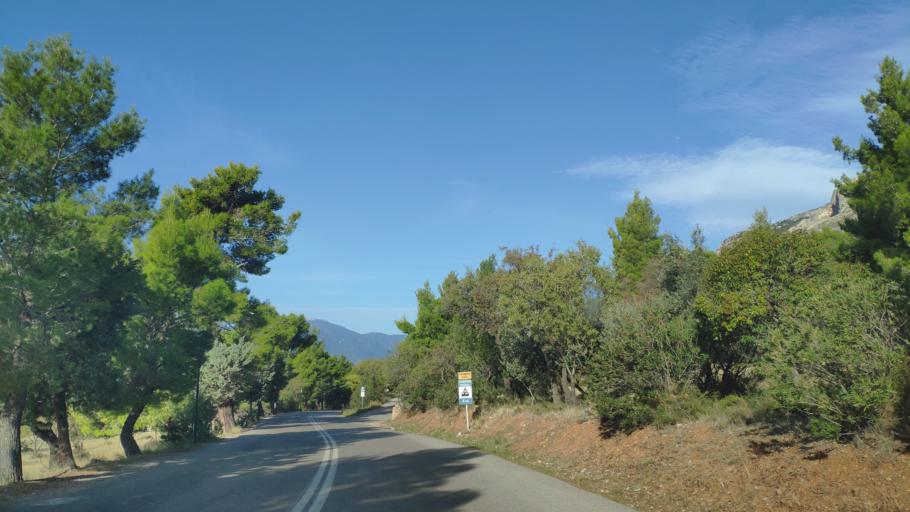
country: GR
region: Central Greece
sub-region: Nomos Fokidos
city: Delphi
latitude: 38.4811
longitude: 22.4875
